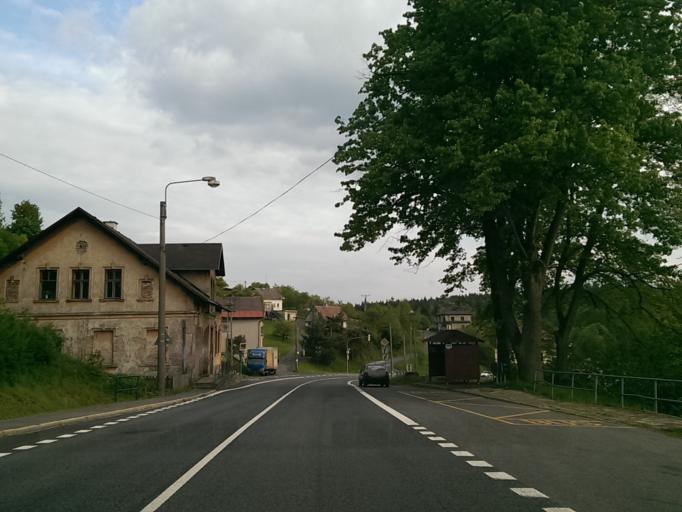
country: CZ
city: Pencin
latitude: 50.6806
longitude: 15.2677
